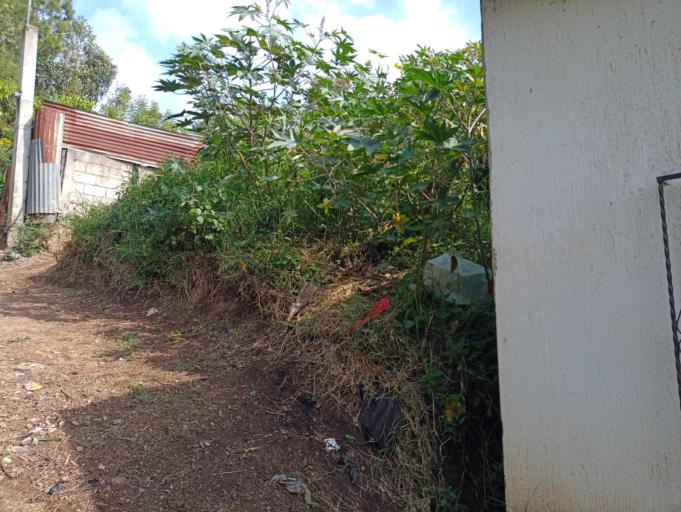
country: GT
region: Guatemala
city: Villa Canales
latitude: 14.4883
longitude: -90.5408
